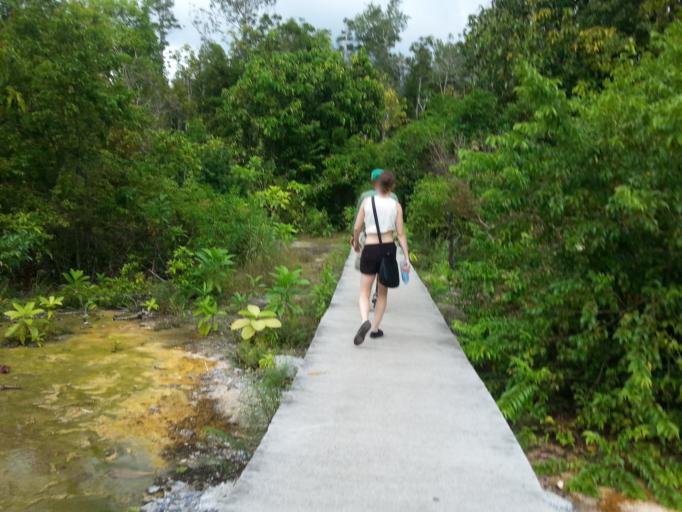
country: TH
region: Krabi
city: Khlong Thom
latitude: 7.9257
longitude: 99.2699
